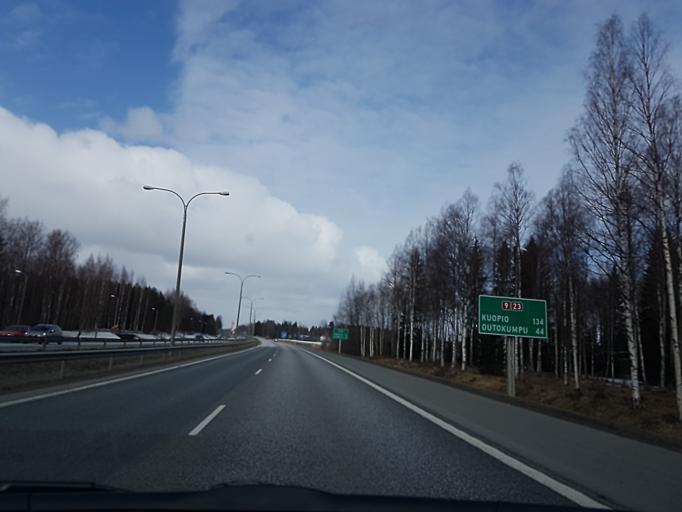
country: FI
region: North Karelia
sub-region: Joensuu
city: Joensuu
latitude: 62.6201
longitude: 29.7254
